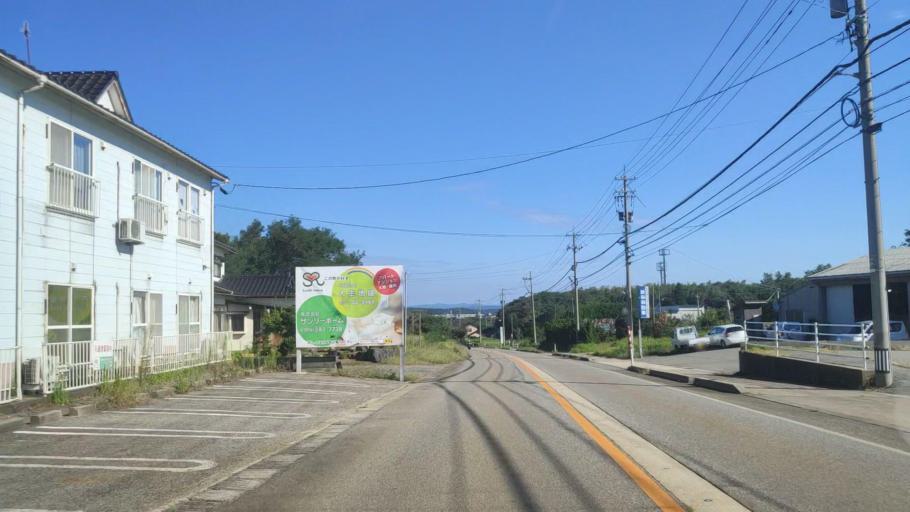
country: JP
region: Ishikawa
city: Hakui
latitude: 36.9910
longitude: 136.7766
